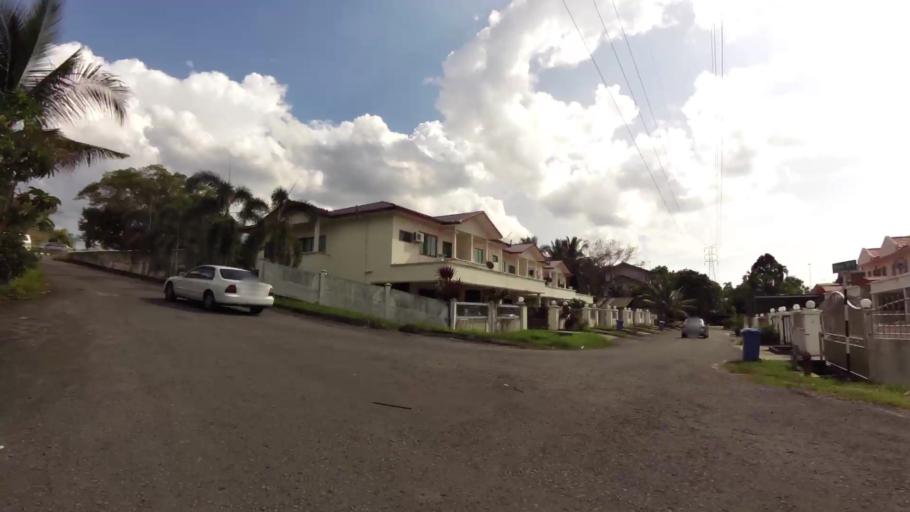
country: BN
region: Brunei and Muara
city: Bandar Seri Begawan
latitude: 4.9507
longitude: 114.9659
